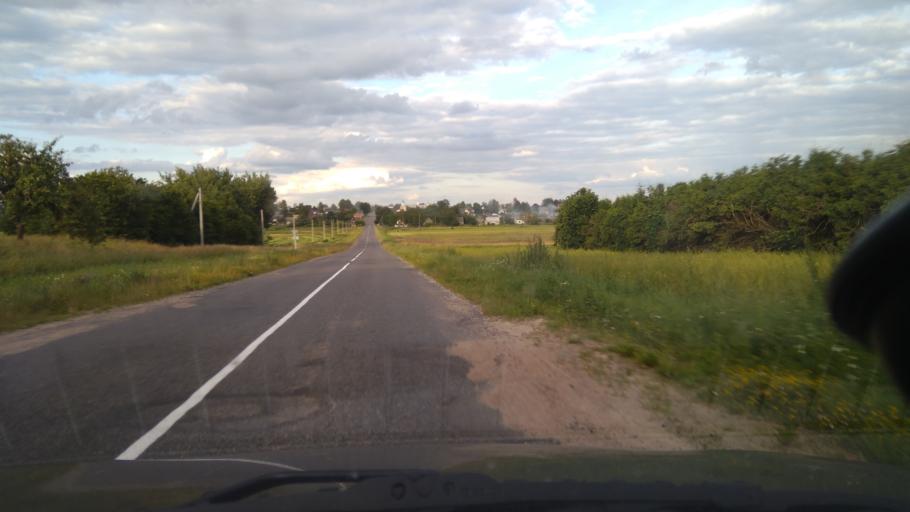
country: BY
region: Grodnenskaya
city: Shchuchin
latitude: 53.5328
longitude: 24.7161
